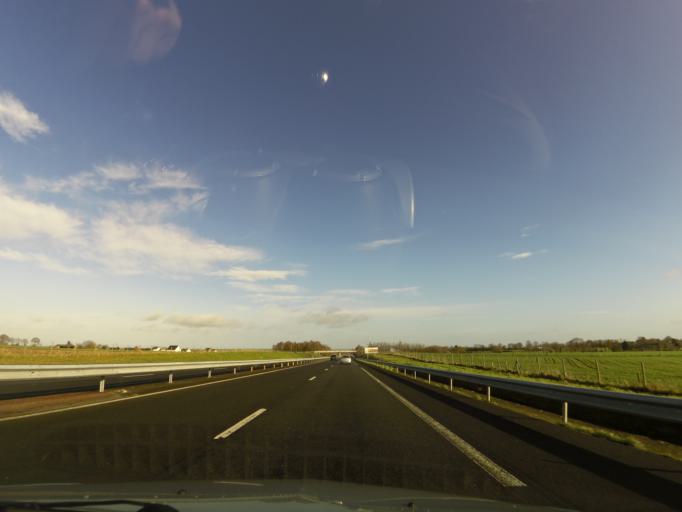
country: FR
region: Lower Normandy
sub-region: Departement de la Manche
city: Saint-James
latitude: 48.5037
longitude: -1.3454
